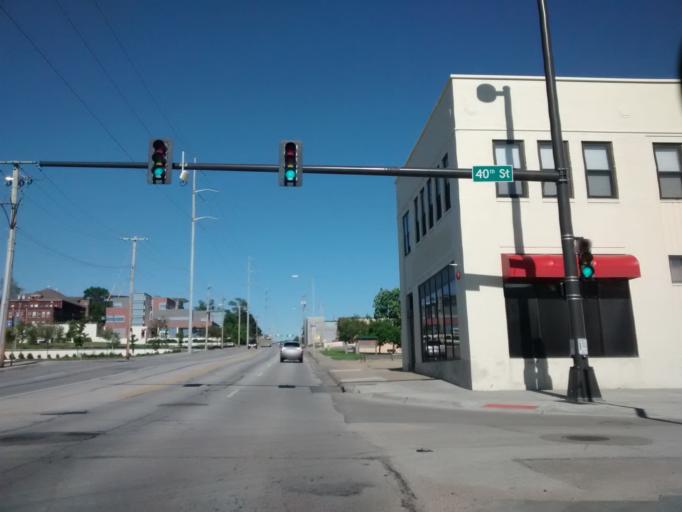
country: US
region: Nebraska
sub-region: Douglas County
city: Omaha
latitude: 41.2524
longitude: -95.9736
